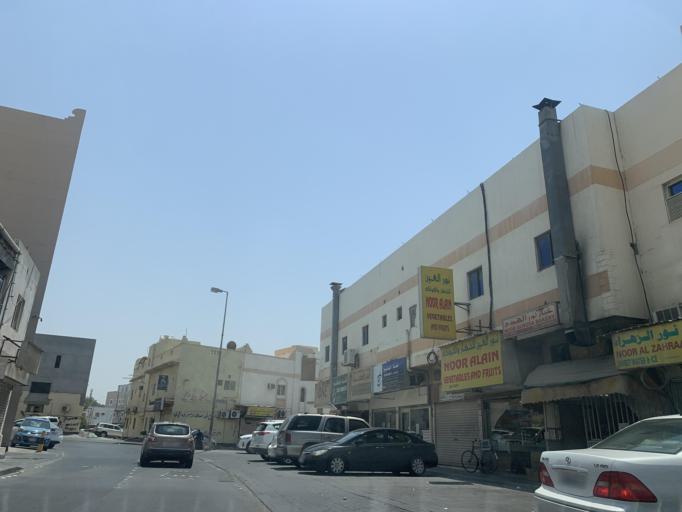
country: BH
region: Manama
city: Jidd Hafs
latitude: 26.2108
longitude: 50.5576
